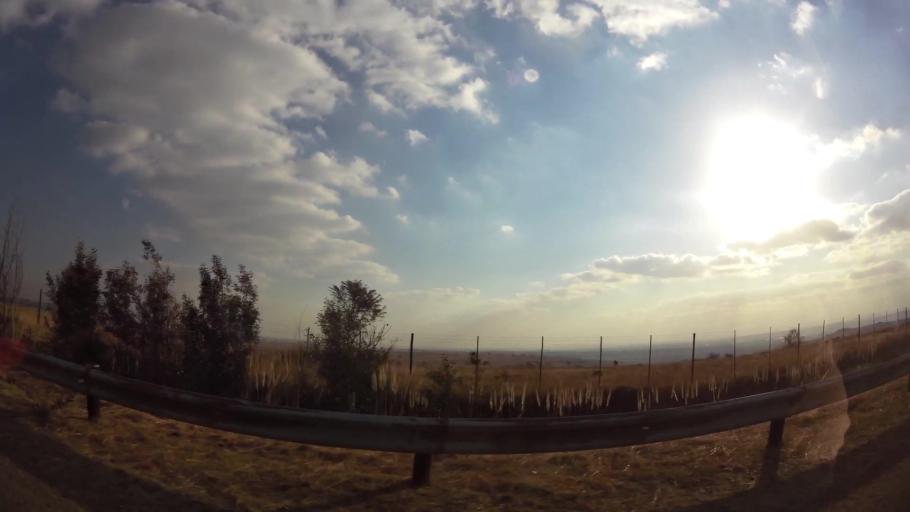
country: ZA
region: Gauteng
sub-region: West Rand District Municipality
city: Krugersdorp
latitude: -26.0946
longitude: 27.7323
